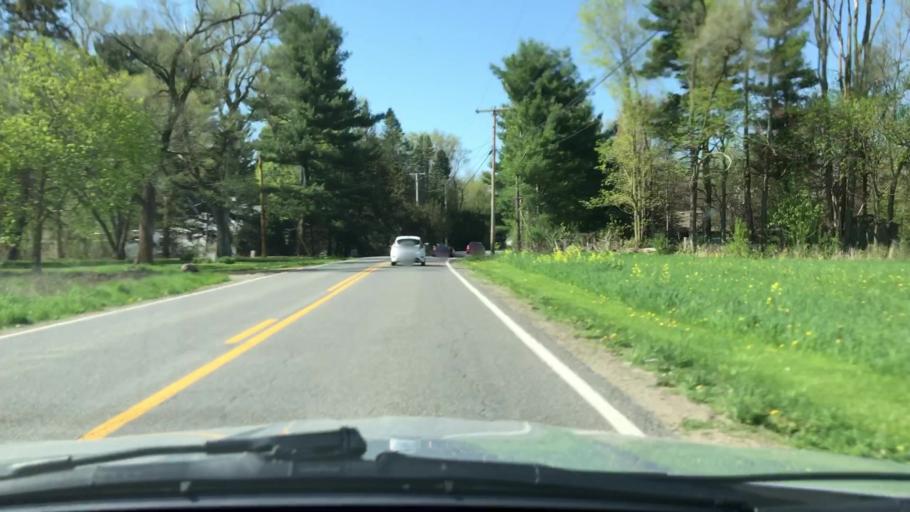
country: US
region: Indiana
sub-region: Saint Joseph County
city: Georgetown
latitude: 41.7570
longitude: -86.3035
